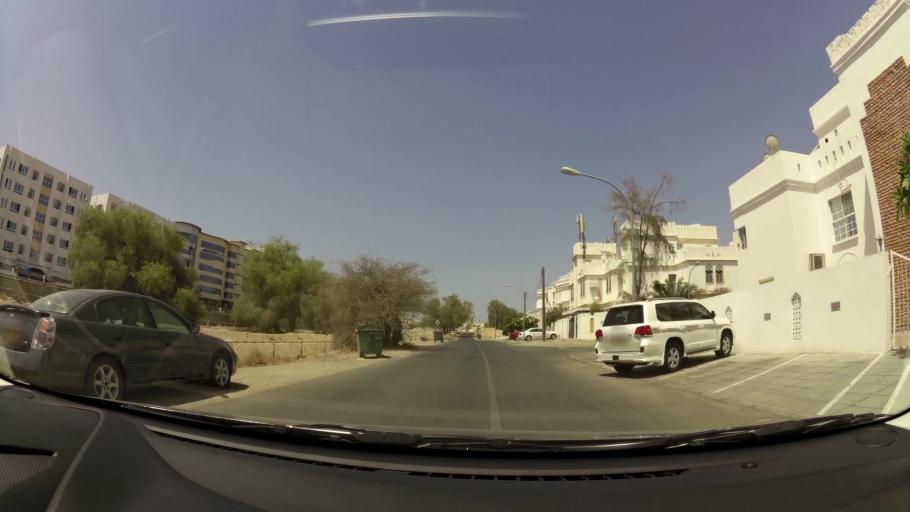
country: OM
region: Muhafazat Masqat
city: Muscat
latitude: 23.6196
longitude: 58.5018
